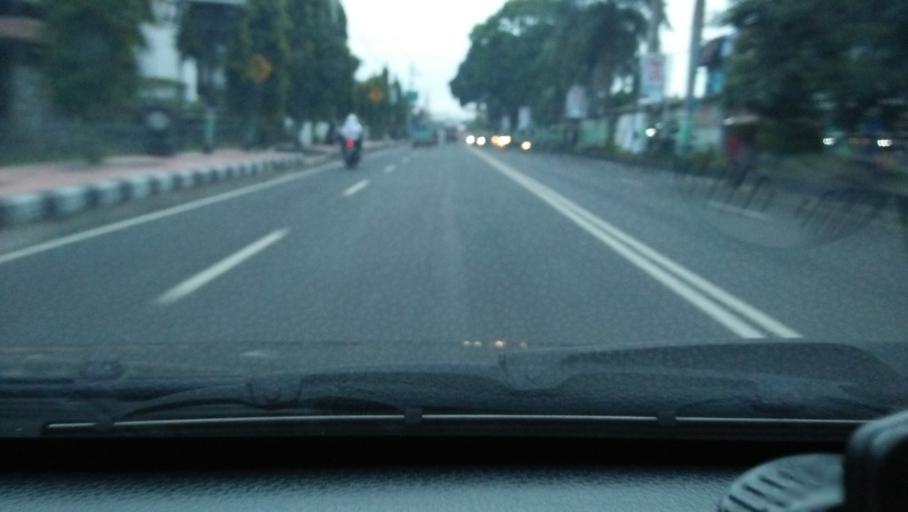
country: ID
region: Central Java
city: Magelang
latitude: -7.4449
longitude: 110.2256
